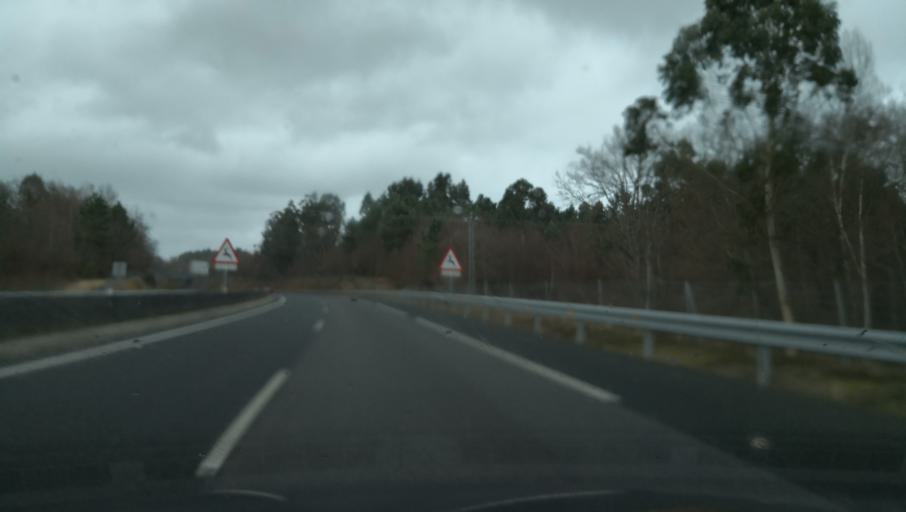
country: ES
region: Galicia
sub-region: Provincia de Pontevedra
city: Lalin
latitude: 42.6793
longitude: -8.1621
